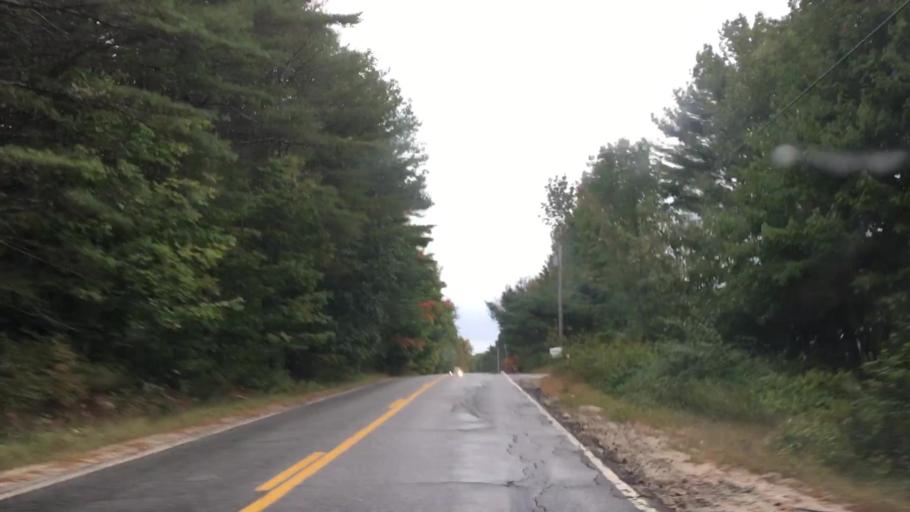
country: US
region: Maine
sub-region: Cumberland County
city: Raymond
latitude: 43.9693
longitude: -70.4676
